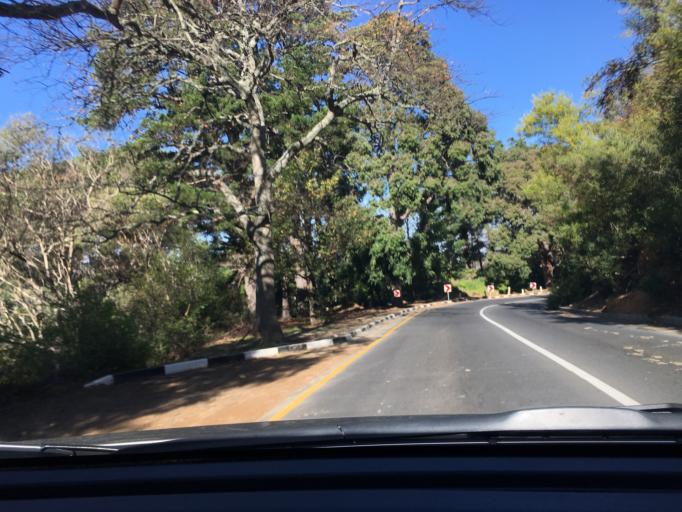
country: ZA
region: Western Cape
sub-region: City of Cape Town
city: Constantia
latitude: -34.0122
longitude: 18.4161
